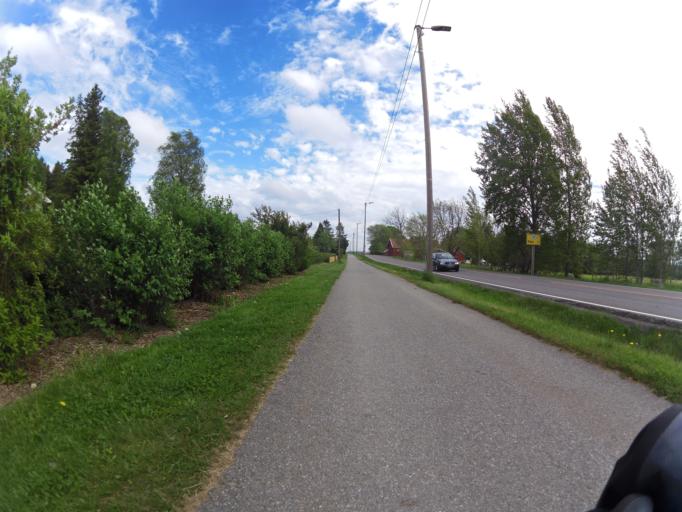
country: NO
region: Ostfold
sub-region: Rygge
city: Ryggebyen
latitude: 59.3702
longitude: 10.7871
